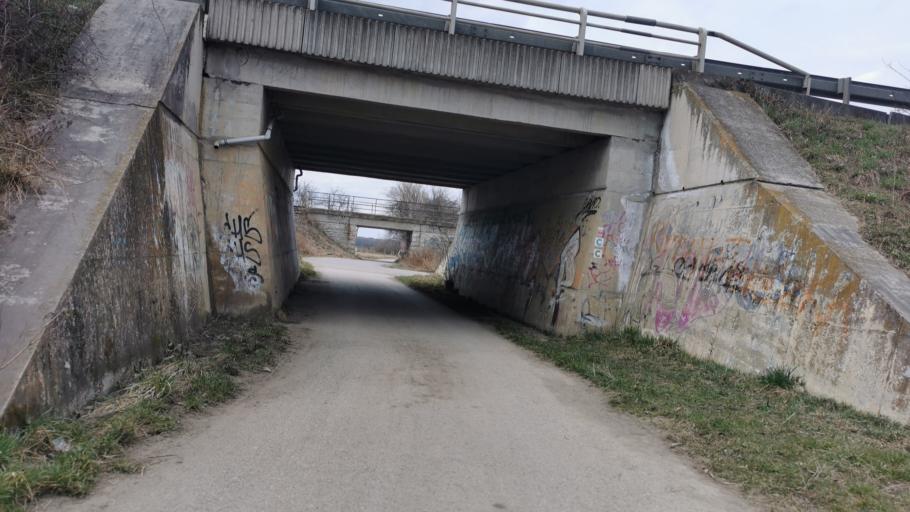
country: SK
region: Trnavsky
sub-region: Okres Skalica
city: Skalica
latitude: 48.8564
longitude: 17.2264
